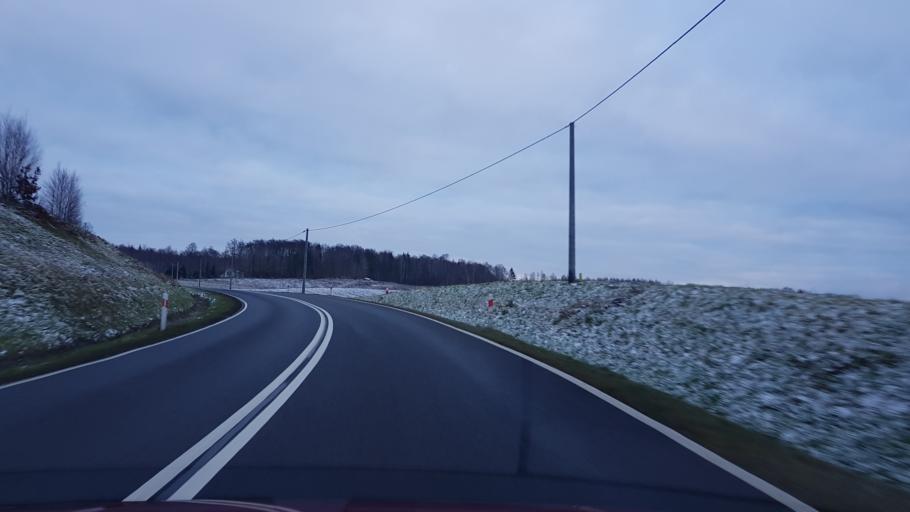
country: PL
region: Pomeranian Voivodeship
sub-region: Powiat bytowski
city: Miastko
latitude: 54.0113
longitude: 17.0390
